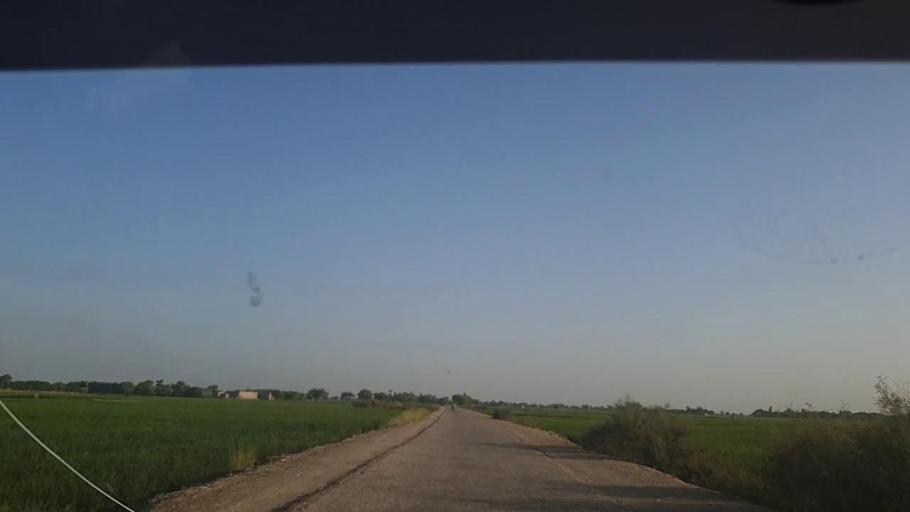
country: PK
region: Sindh
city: Thul
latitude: 28.2140
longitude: 68.8695
